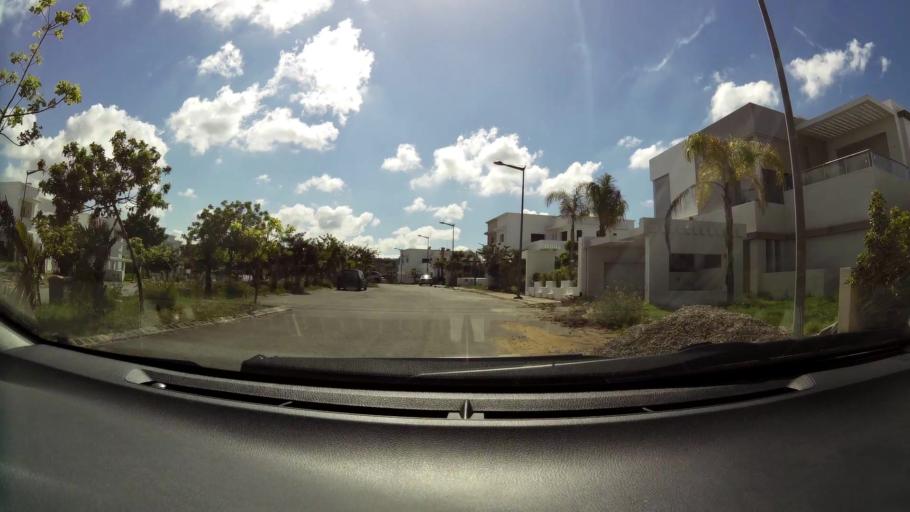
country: MA
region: Grand Casablanca
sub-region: Nouaceur
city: Bouskoura
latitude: 33.4665
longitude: -7.5954
